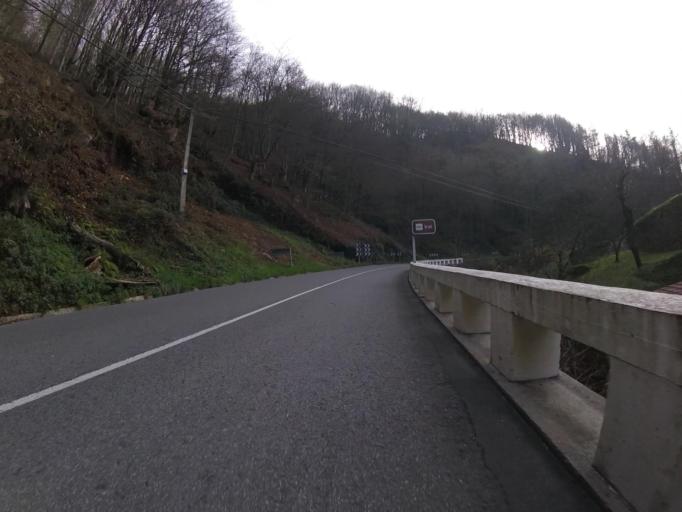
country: ES
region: Basque Country
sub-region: Provincia de Guipuzcoa
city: Berastegui
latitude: 43.1361
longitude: -1.9865
